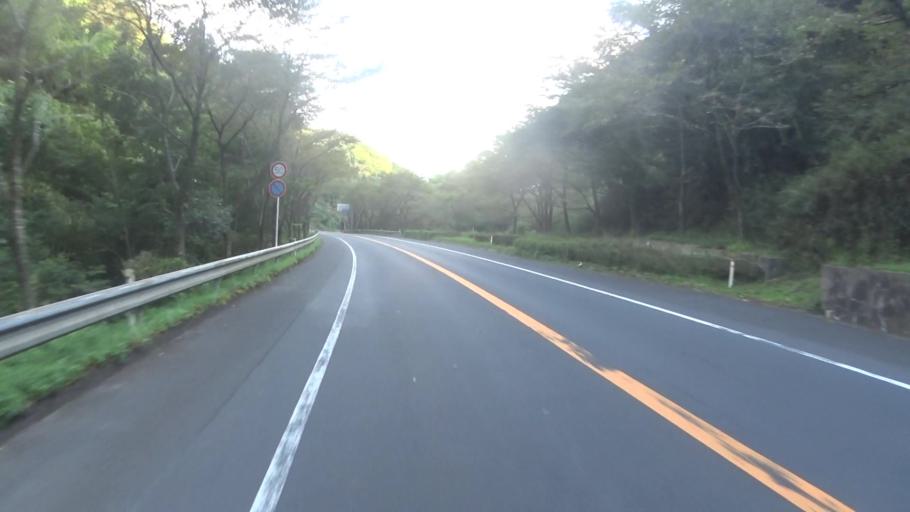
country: JP
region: Kyoto
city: Miyazu
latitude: 35.5468
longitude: 135.1107
